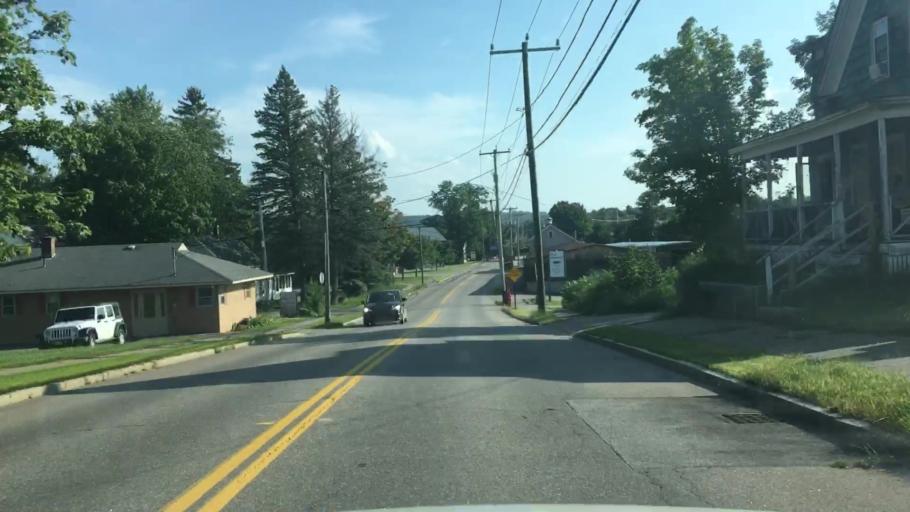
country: US
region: New Hampshire
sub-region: Belknap County
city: Laconia
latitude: 43.5398
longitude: -71.4662
